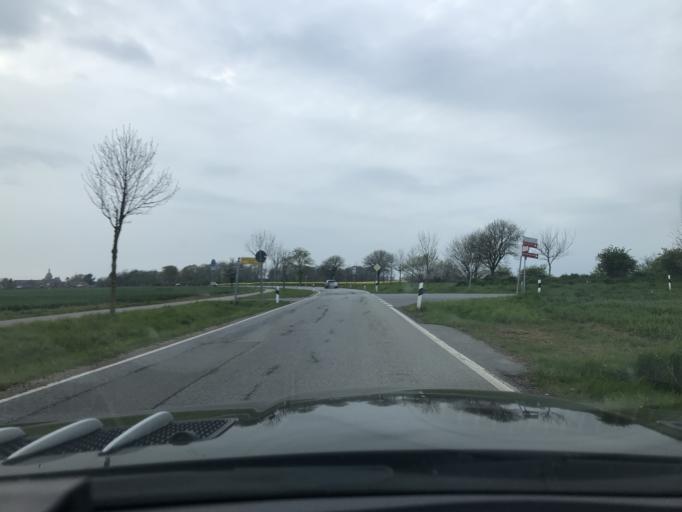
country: DE
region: Schleswig-Holstein
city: Burg auf Fehmarn
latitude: 54.4326
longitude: 11.2151
